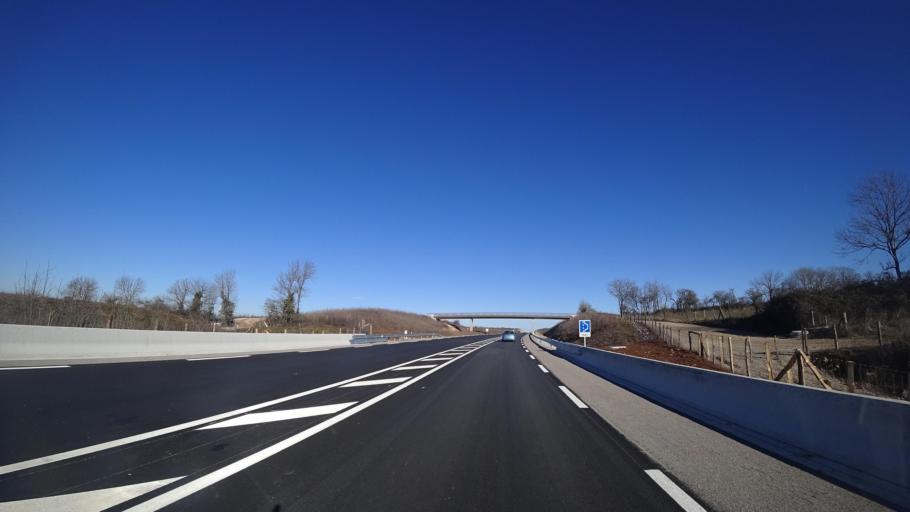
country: FR
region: Midi-Pyrenees
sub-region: Departement de l'Aveyron
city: Sebazac-Concoures
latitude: 44.3923
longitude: 2.6143
